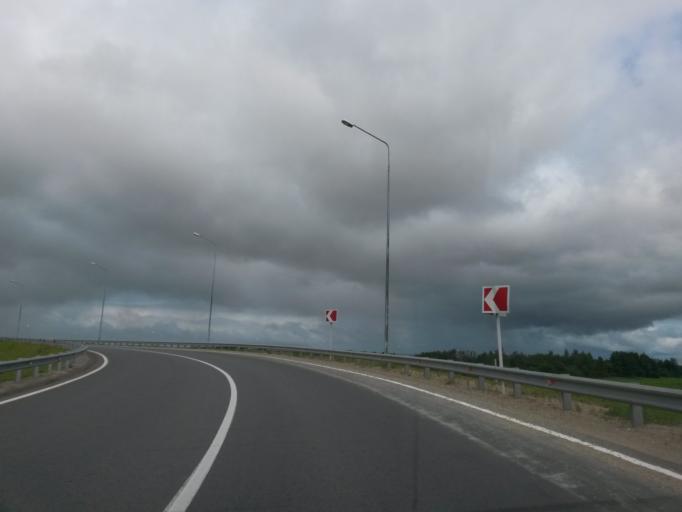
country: RU
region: Jaroslavl
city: Yaroslavl
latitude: 57.7384
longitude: 39.8997
